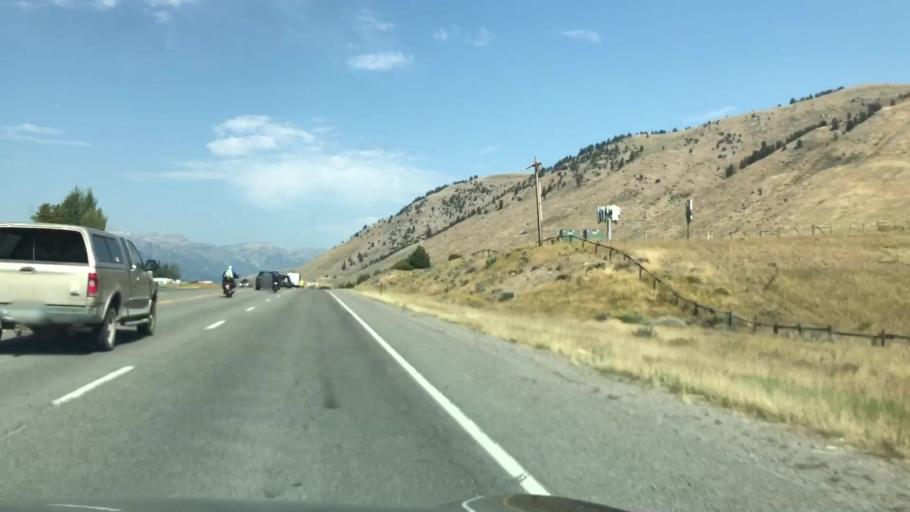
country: US
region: Wyoming
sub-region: Teton County
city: South Park
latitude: 43.4175
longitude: -110.7743
